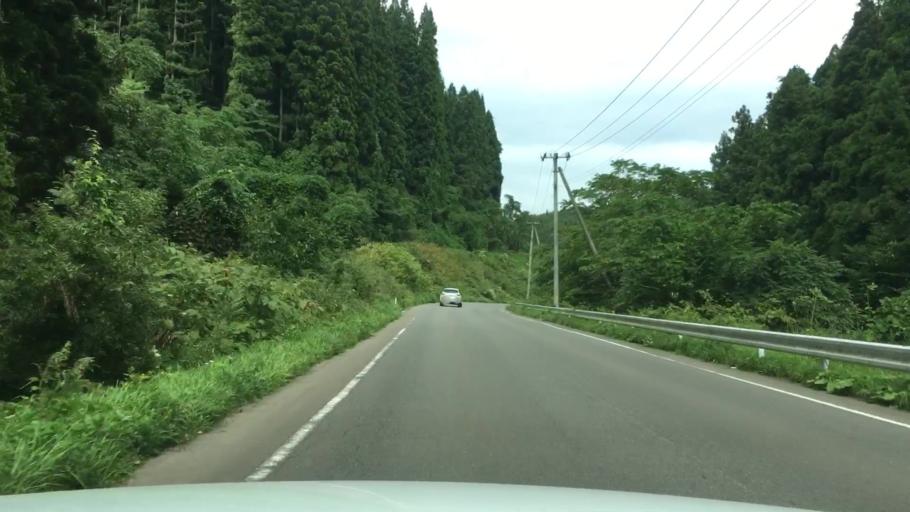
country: JP
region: Aomori
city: Shimokizukuri
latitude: 40.7394
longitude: 140.2452
